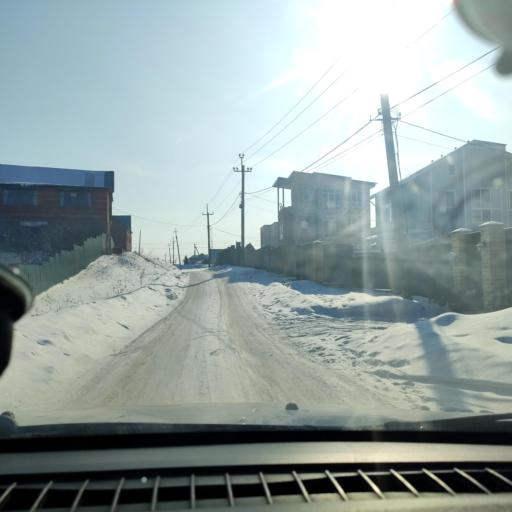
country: RU
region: Bashkortostan
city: Kabakovo
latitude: 54.5031
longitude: 55.9085
